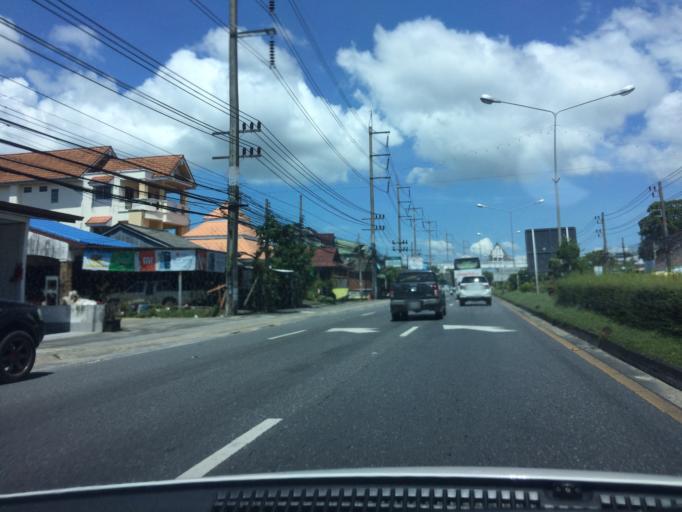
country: TH
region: Phuket
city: Thalang
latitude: 8.0326
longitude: 98.3333
